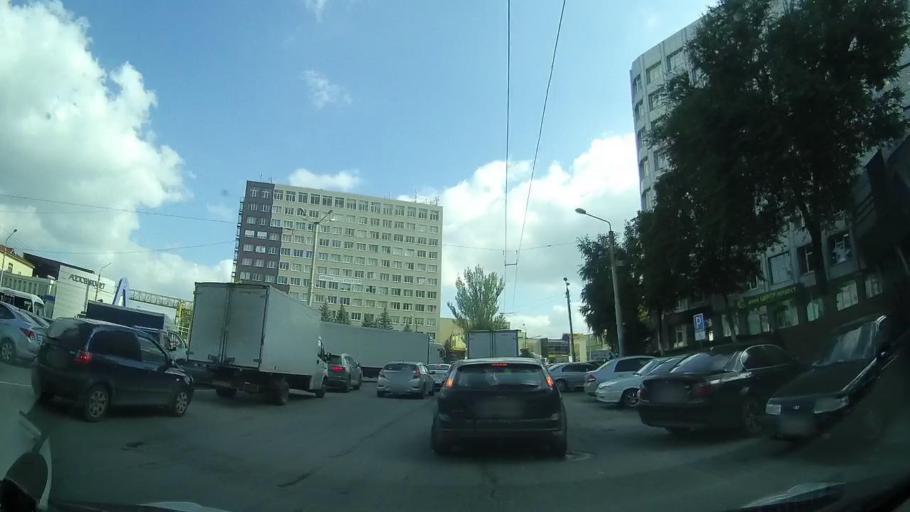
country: RU
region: Rostov
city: Imeni Chkalova
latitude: 47.2720
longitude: 39.7617
